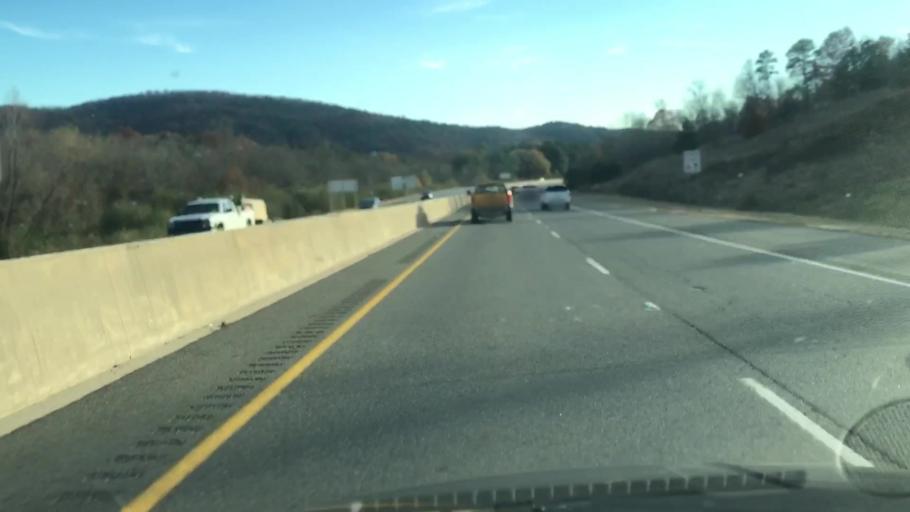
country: US
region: Arkansas
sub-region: Garland County
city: Hot Springs
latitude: 34.4973
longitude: -92.9756
